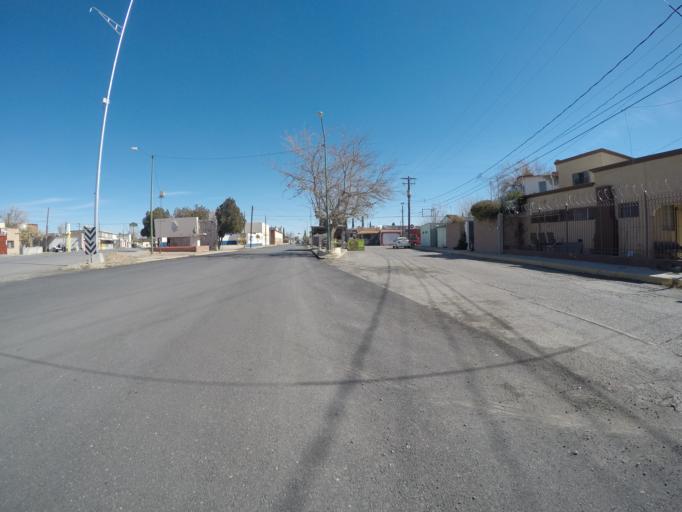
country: MX
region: Chihuahua
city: Ciudad Juarez
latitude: 31.7409
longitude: -106.4715
